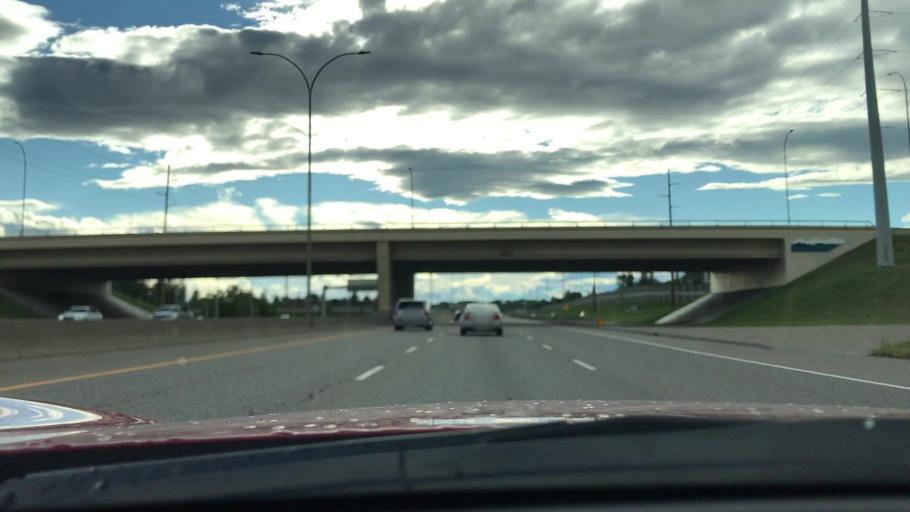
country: CA
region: Alberta
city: Calgary
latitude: 50.9486
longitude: -114.0029
